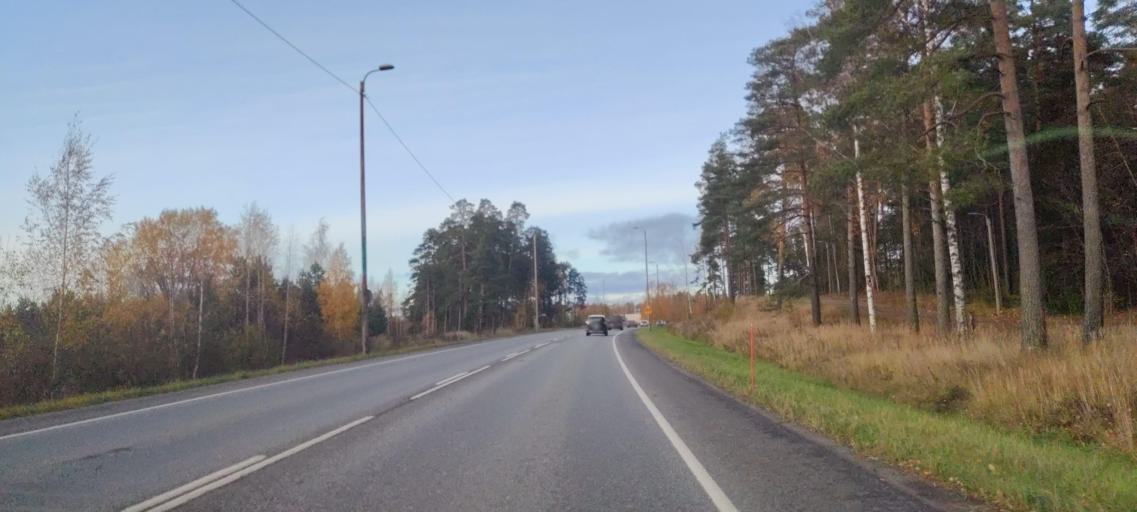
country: FI
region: Satakunta
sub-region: Pori
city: Pori
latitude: 61.4734
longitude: 21.7568
